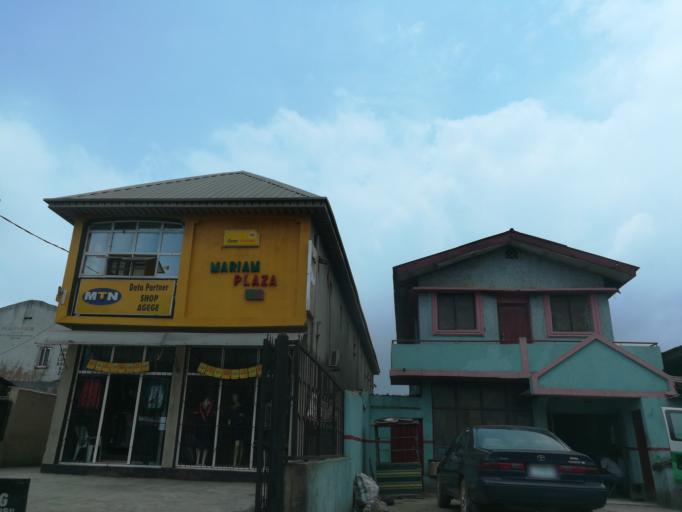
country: NG
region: Lagos
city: Agege
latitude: 6.6245
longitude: 3.3236
